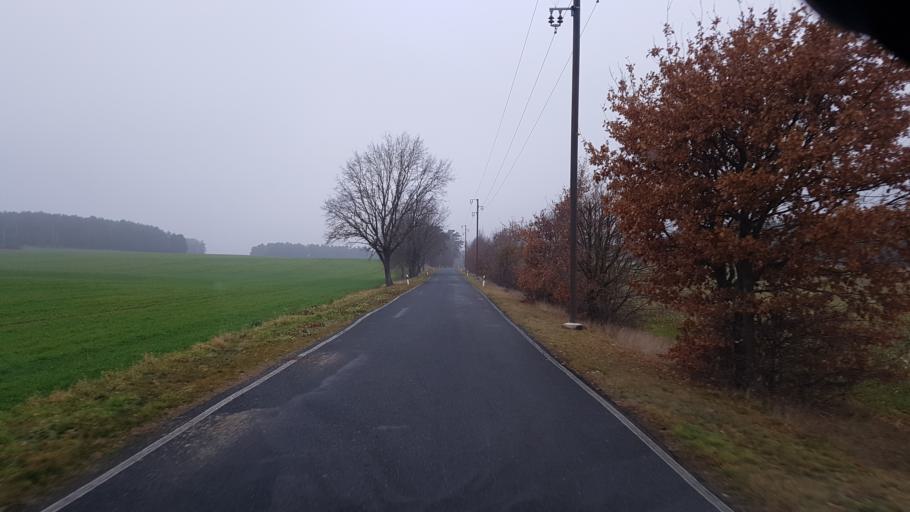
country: DE
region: Brandenburg
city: Altdobern
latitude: 51.6789
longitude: 13.9837
